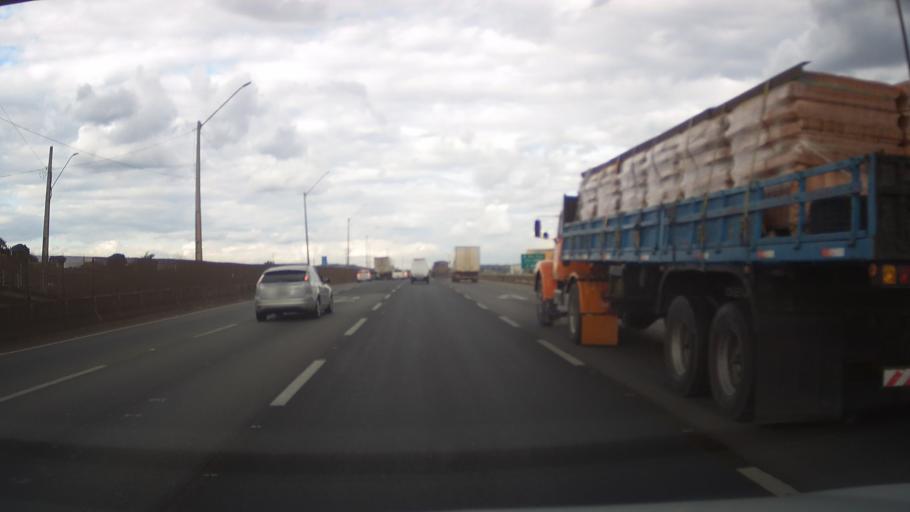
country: BR
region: Minas Gerais
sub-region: Betim
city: Betim
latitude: -19.9588
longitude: -44.1514
